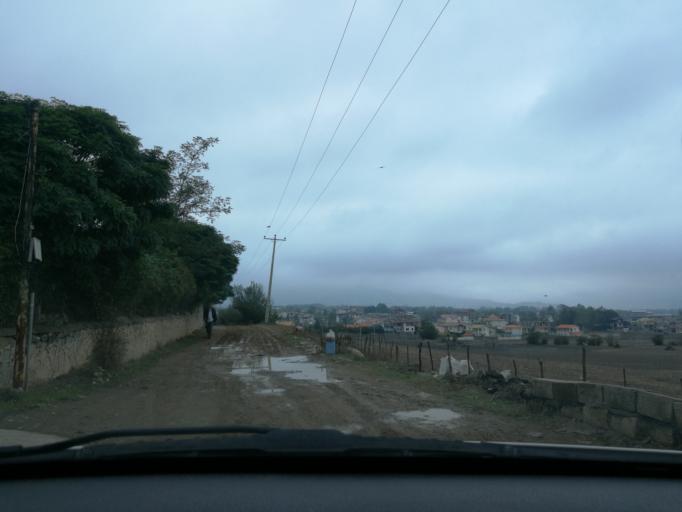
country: IR
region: Mazandaran
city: `Abbasabad
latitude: 36.5027
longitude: 51.2061
